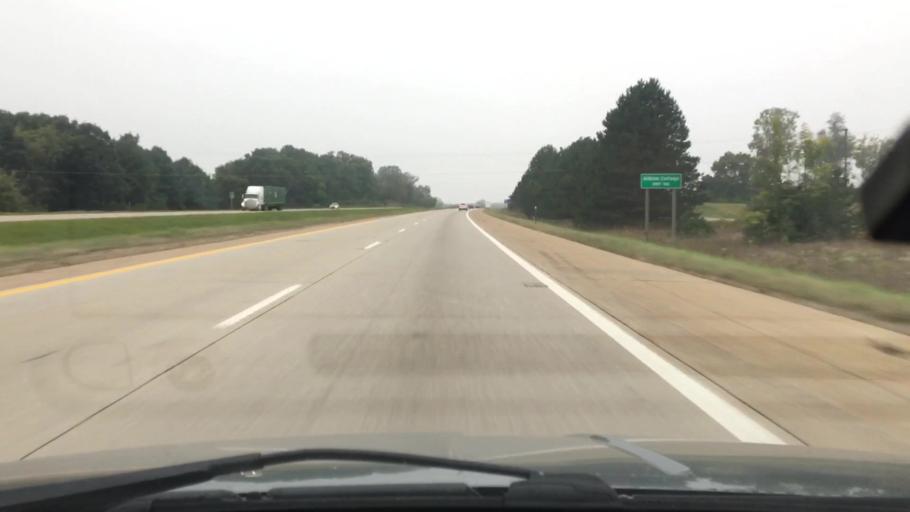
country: US
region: Michigan
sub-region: Calhoun County
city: Albion
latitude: 42.2621
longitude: -84.6953
